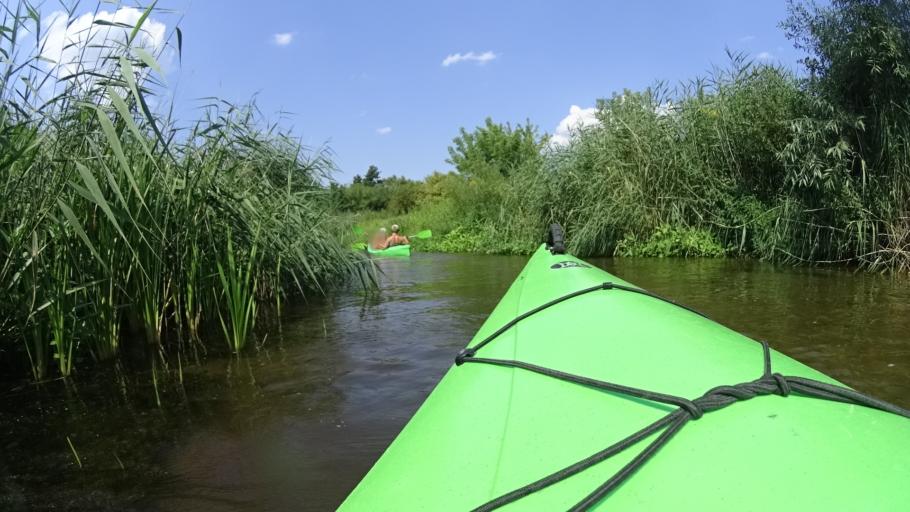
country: PL
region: Masovian Voivodeship
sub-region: Powiat bialobrzeski
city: Wysmierzyce
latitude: 51.6528
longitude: 20.8225
